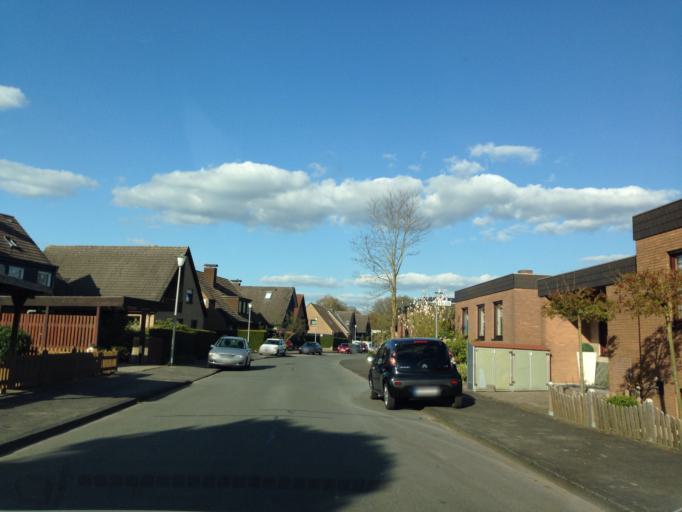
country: DE
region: North Rhine-Westphalia
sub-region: Regierungsbezirk Munster
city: Muenster
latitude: 52.0009
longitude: 7.5903
